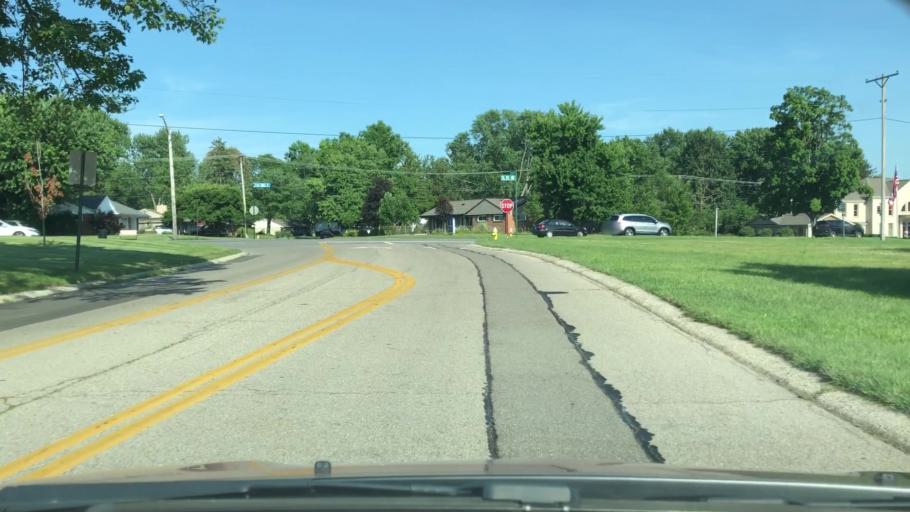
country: US
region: Ohio
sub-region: Montgomery County
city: Centerville
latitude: 39.6414
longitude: -84.1585
